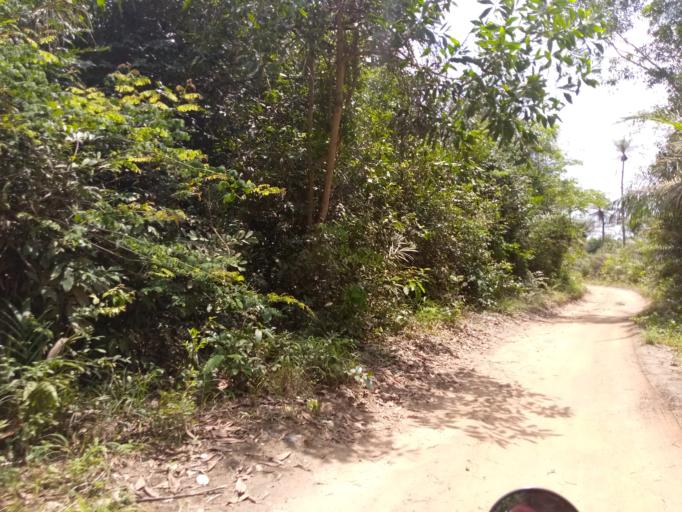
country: SL
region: Western Area
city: Waterloo
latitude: 8.3729
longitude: -12.9993
